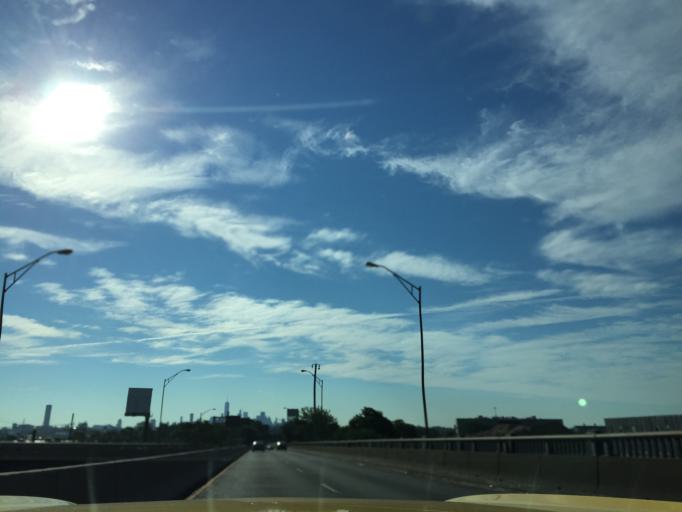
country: US
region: New Jersey
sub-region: Hudson County
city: Jersey City
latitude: 40.7318
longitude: -74.1150
